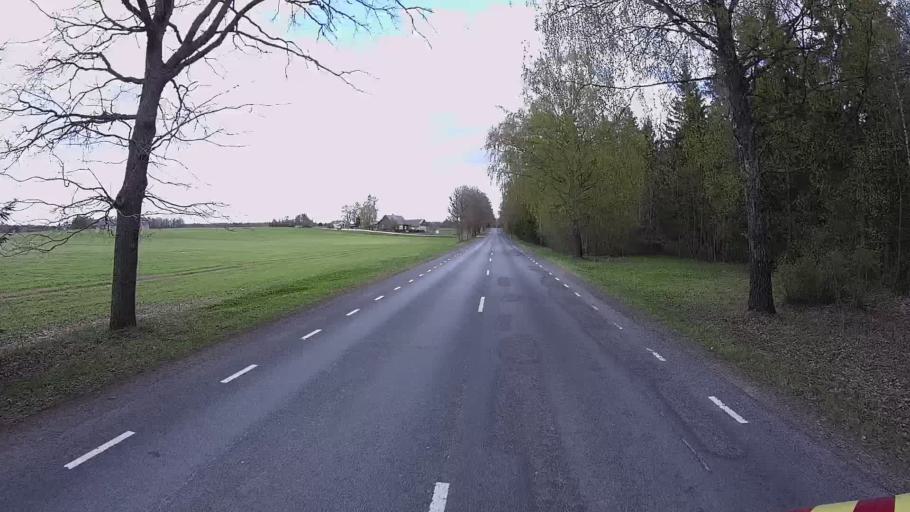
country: EE
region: Jaervamaa
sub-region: Koeru vald
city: Koeru
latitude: 58.9740
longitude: 26.0374
